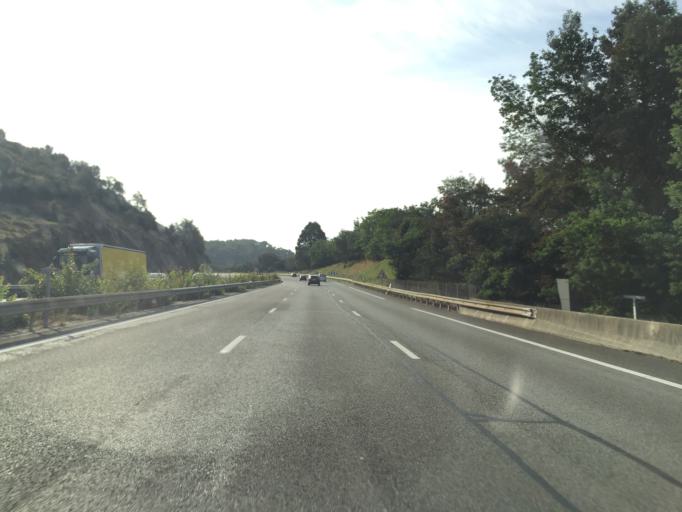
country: FR
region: Provence-Alpes-Cote d'Azur
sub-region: Departement du Var
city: Tanneron
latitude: 43.5392
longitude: 6.8559
